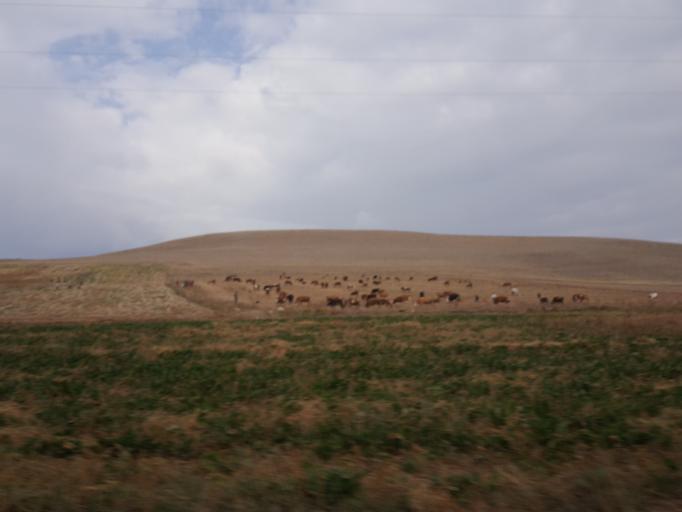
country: TR
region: Corum
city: Cemilbey
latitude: 40.2258
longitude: 35.0468
